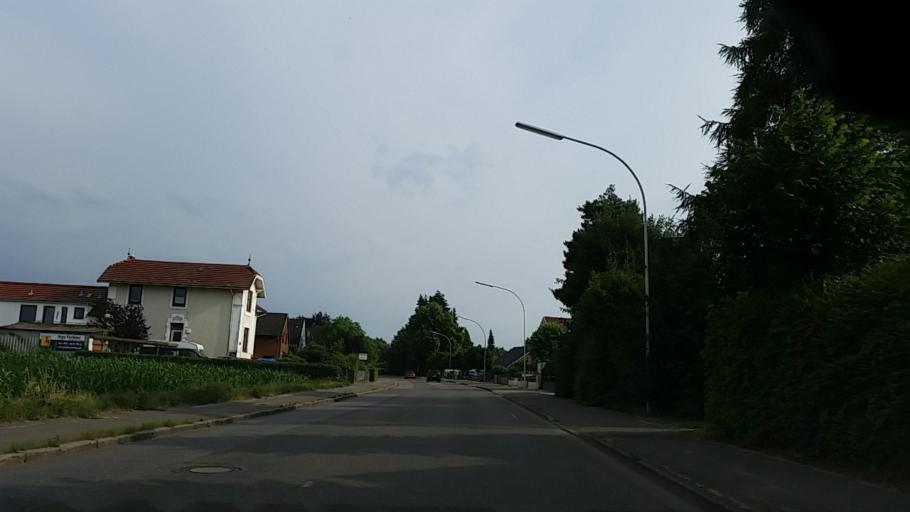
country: DE
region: Schleswig-Holstein
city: Halstenbek
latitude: 53.5955
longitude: 9.8222
